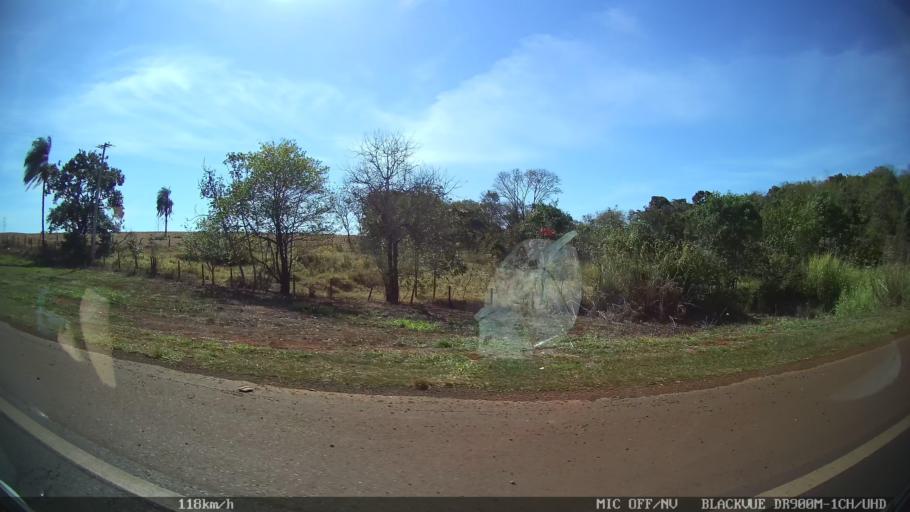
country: BR
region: Sao Paulo
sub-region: Ipua
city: Ipua
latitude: -20.4600
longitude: -48.1452
